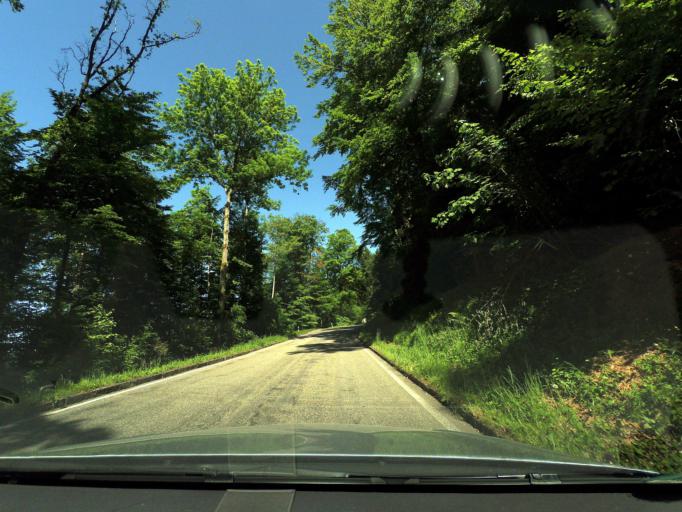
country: DE
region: Baden-Wuerttemberg
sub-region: Regierungsbezirk Stuttgart
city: Murrhardt
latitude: 48.9720
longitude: 9.5805
